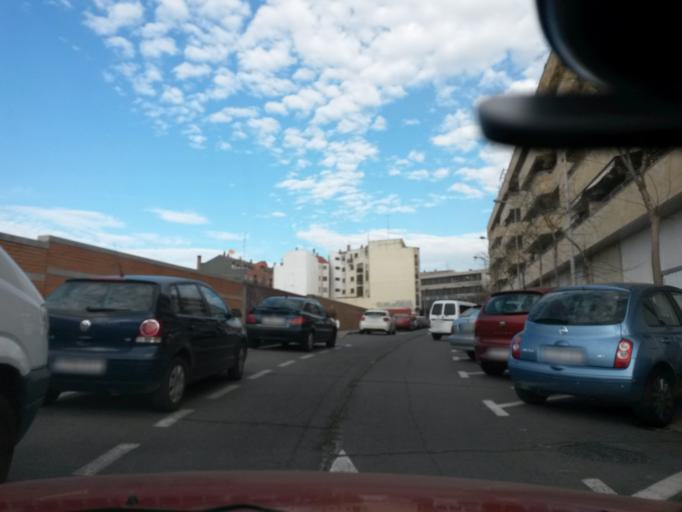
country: ES
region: Castille and Leon
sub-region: Provincia de Salamanca
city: Salamanca
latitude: 40.9607
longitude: -5.6534
